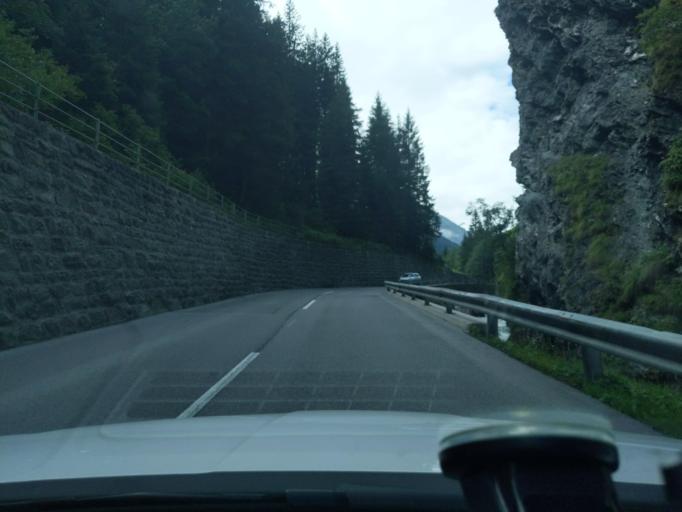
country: AT
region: Tyrol
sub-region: Politischer Bezirk Schwaz
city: Schwendau
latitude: 47.1487
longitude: 11.7213
